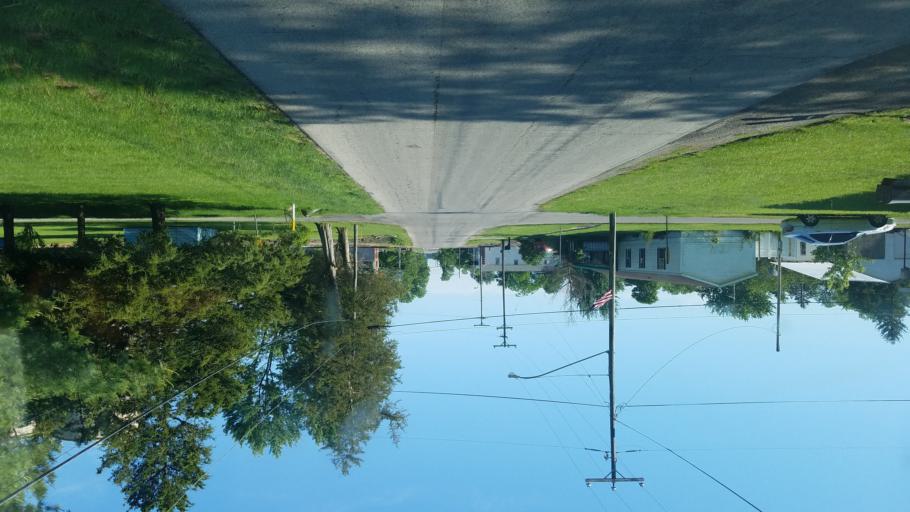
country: US
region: Ohio
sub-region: Union County
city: Richwood
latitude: 40.5868
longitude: -83.3149
